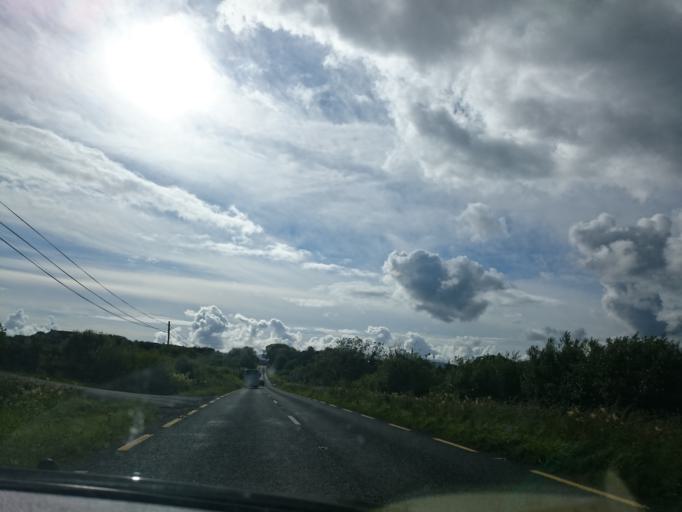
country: IE
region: Connaught
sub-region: Maigh Eo
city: Westport
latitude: 53.9015
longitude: -9.6029
